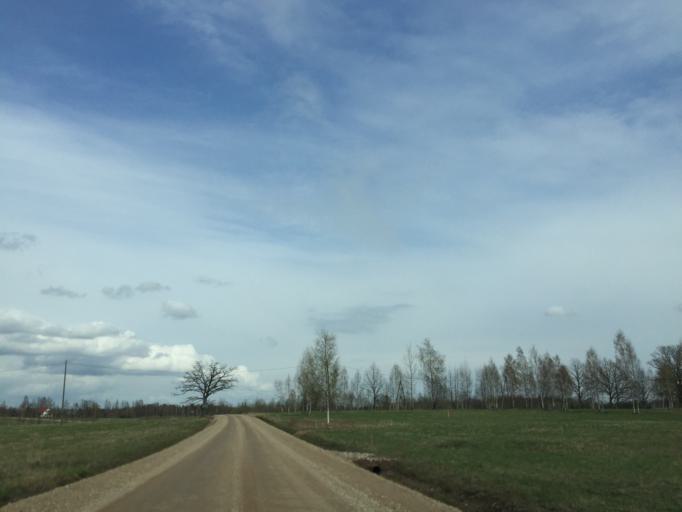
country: LV
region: Ligatne
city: Ligatne
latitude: 57.2092
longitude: 25.0610
